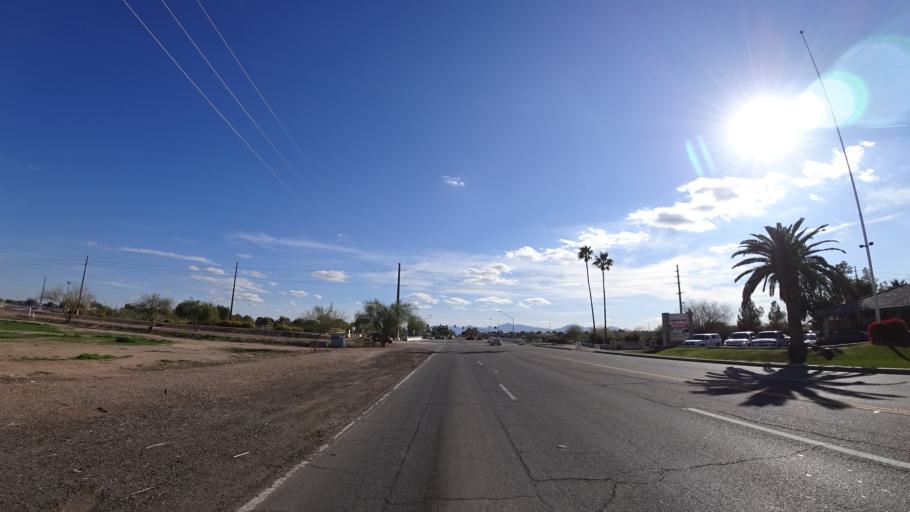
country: US
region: Arizona
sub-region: Maricopa County
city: Glendale
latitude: 33.5241
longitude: -112.2376
